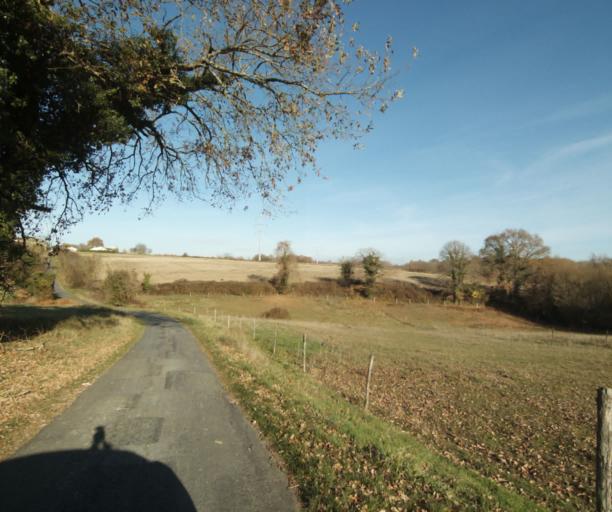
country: FR
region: Poitou-Charentes
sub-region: Departement de la Charente-Maritime
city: Ecoyeux
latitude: 45.7731
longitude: -0.5036
